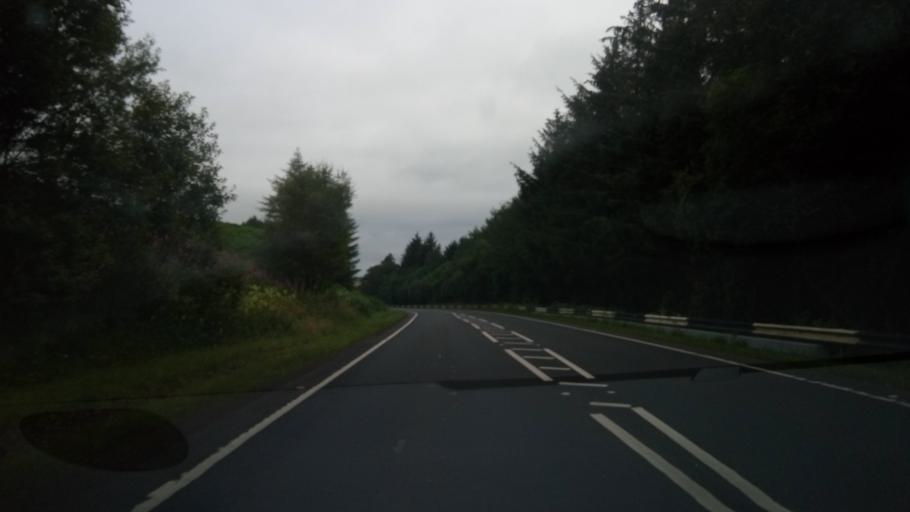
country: GB
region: Scotland
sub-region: The Scottish Borders
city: Hawick
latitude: 55.3588
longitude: -2.8980
